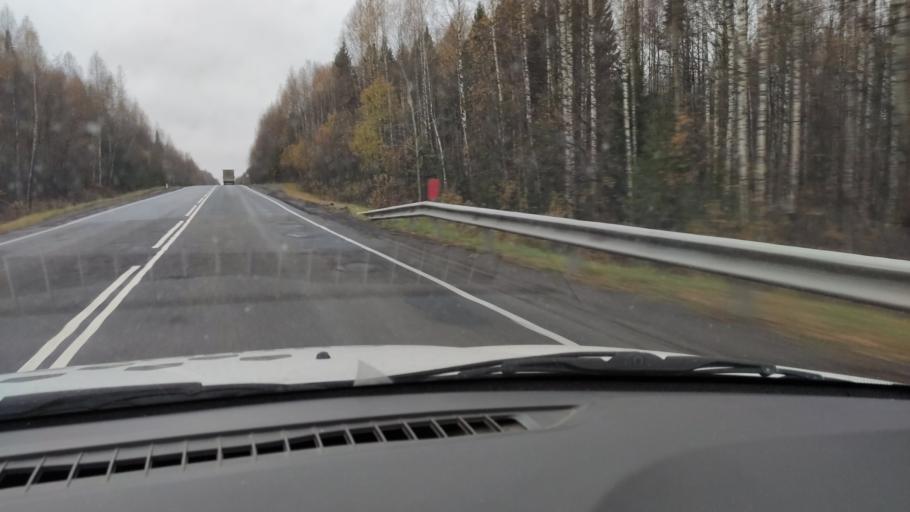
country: RU
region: Kirov
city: Omutninsk
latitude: 58.7638
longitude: 51.9939
